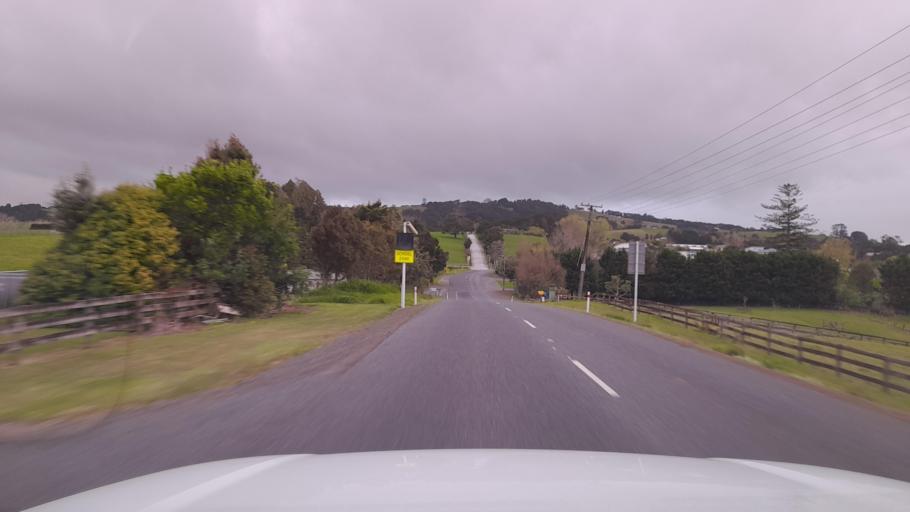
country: NZ
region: Northland
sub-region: Whangarei
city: Maungatapere
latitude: -35.6596
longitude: 174.2238
